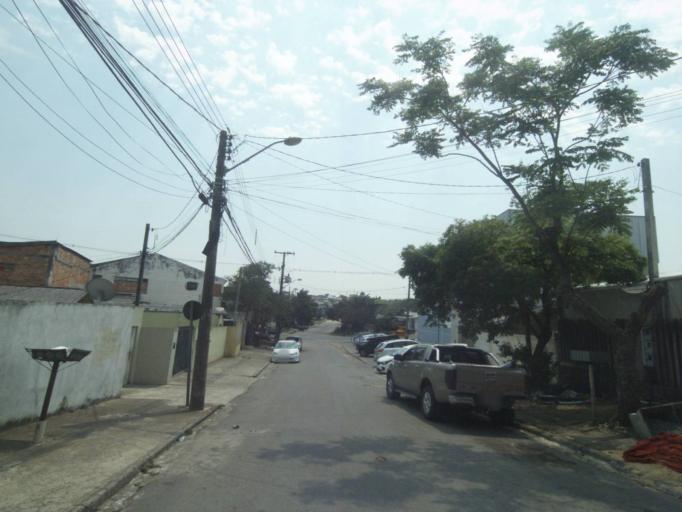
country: BR
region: Parana
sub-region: Sao Jose Dos Pinhais
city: Sao Jose dos Pinhais
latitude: -25.5361
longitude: -49.2502
